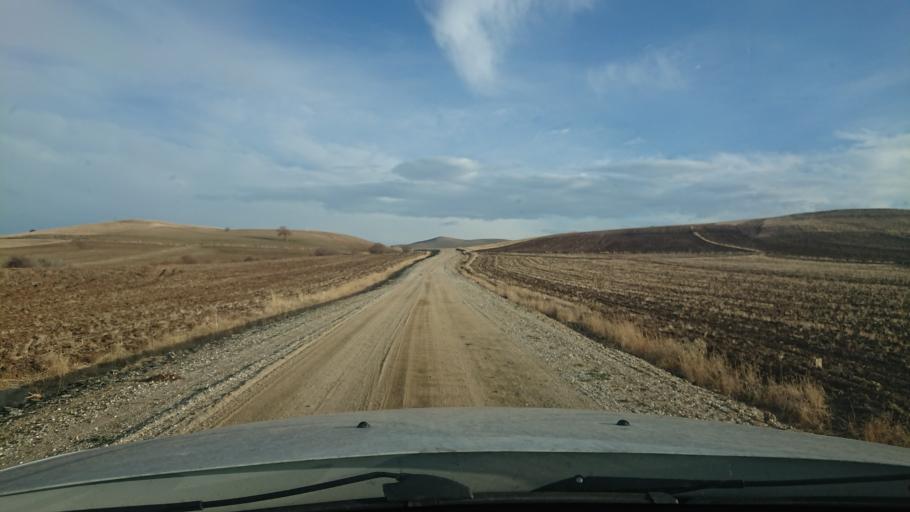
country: TR
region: Aksaray
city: Acipinar
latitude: 38.6944
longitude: 33.8706
